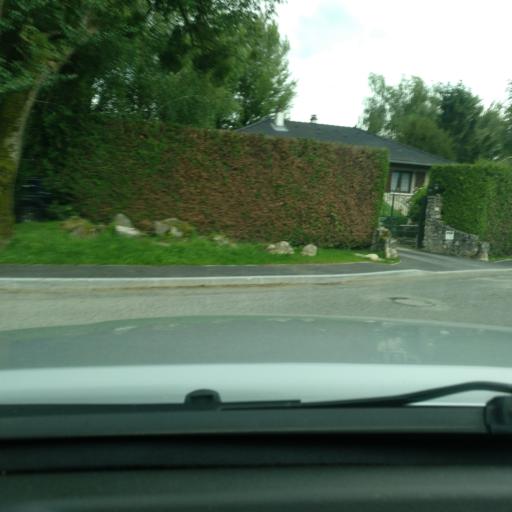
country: FR
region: Rhone-Alpes
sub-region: Departement de la Haute-Savoie
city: Amancy
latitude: 46.0769
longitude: 6.3605
